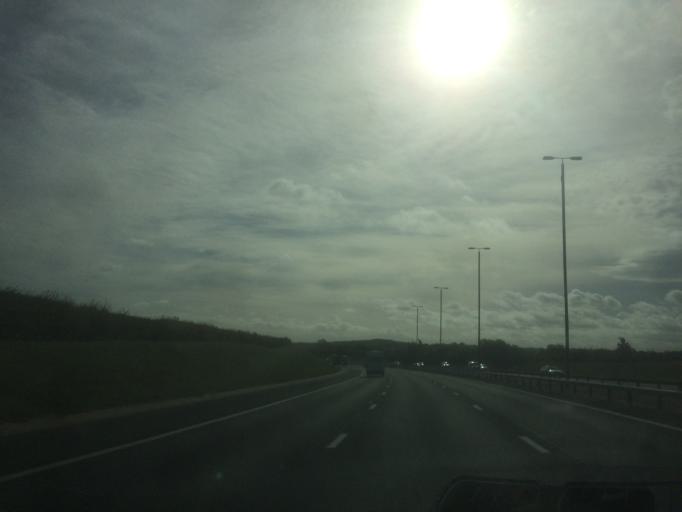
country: GB
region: England
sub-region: City and Borough of Leeds
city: Aberford
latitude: 53.8038
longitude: -1.3376
